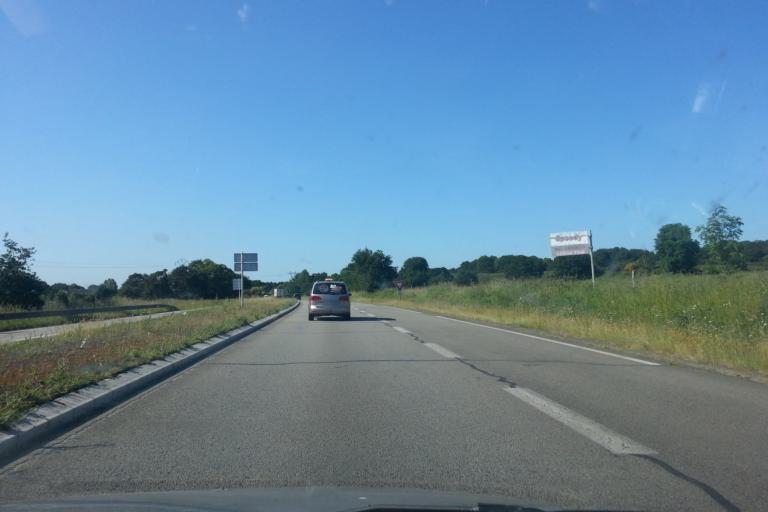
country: FR
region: Brittany
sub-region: Departement du Morbihan
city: Caudan
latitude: 47.7977
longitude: -3.3402
